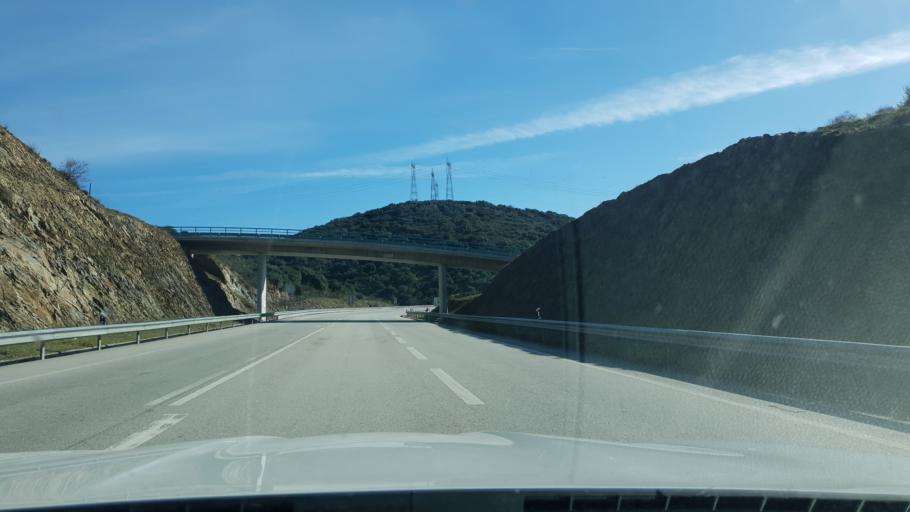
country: PT
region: Braganca
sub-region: Torre de Moncorvo
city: Torre de Moncorvo
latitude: 41.1829
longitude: -7.0814
